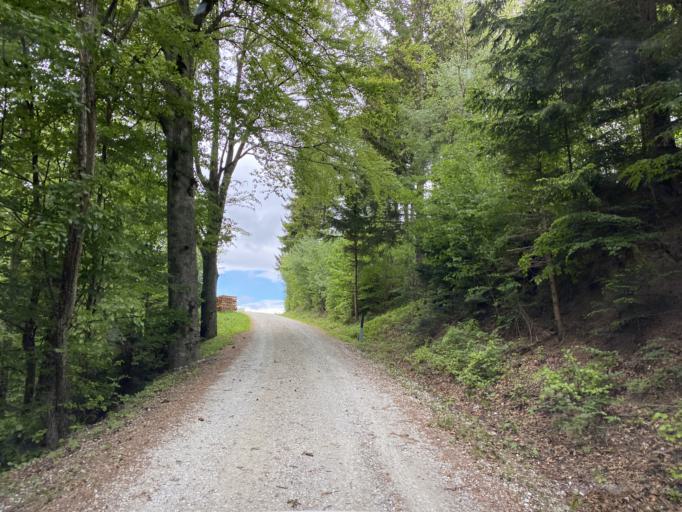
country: AT
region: Styria
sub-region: Politischer Bezirk Weiz
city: Baierdorf-Umgebung
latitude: 47.2972
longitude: 15.7009
